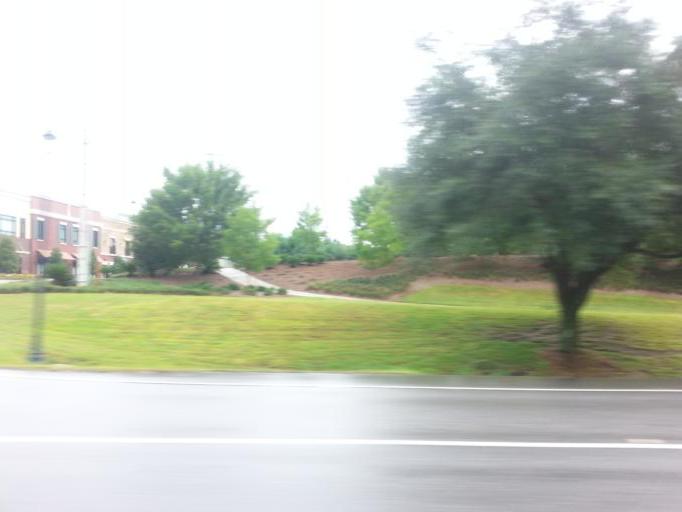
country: US
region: Alabama
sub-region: Baldwin County
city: Fairhope
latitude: 30.5540
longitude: -87.8924
